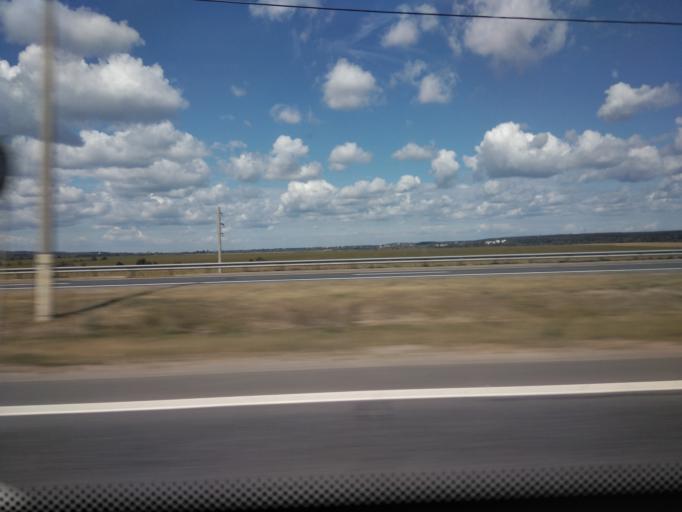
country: RU
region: Moskovskaya
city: Danki
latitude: 54.8776
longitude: 37.5082
